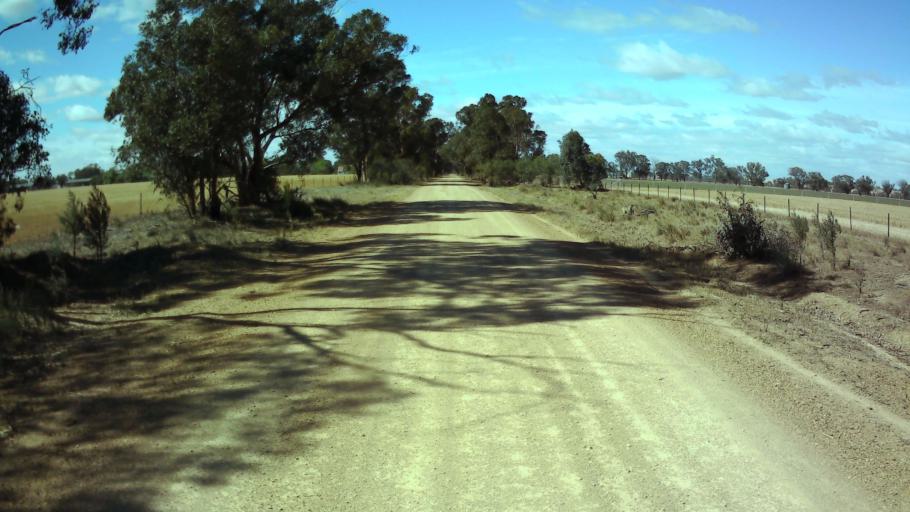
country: AU
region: New South Wales
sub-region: Weddin
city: Grenfell
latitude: -34.0388
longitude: 148.3161
